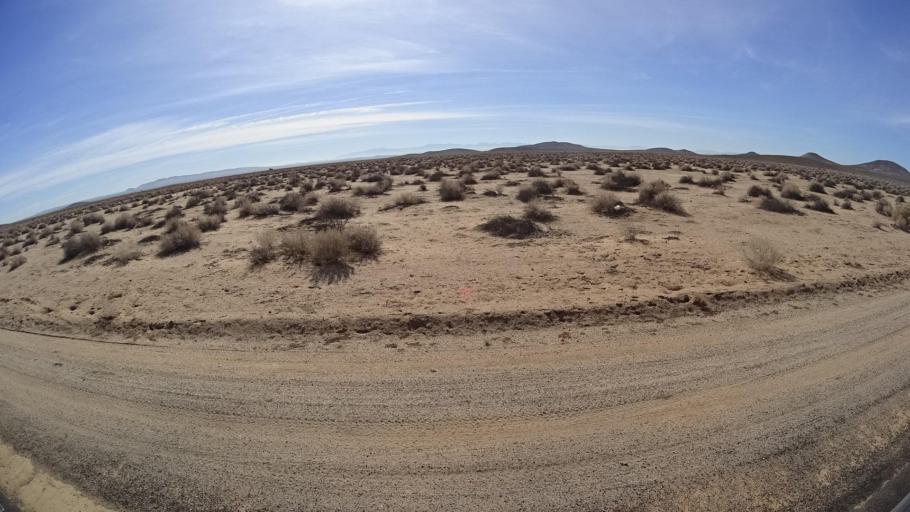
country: US
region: California
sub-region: Kern County
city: North Edwards
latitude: 35.0728
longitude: -117.7977
